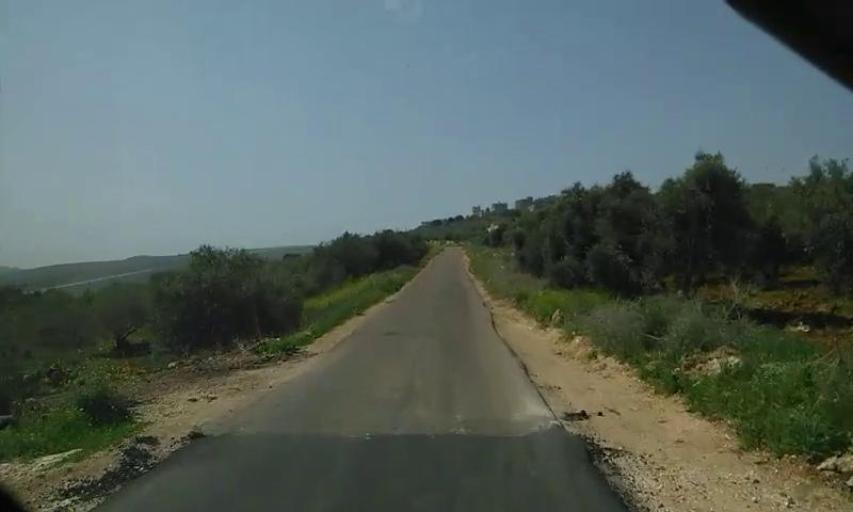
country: PS
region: West Bank
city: `Anin
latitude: 32.4976
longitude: 35.1822
